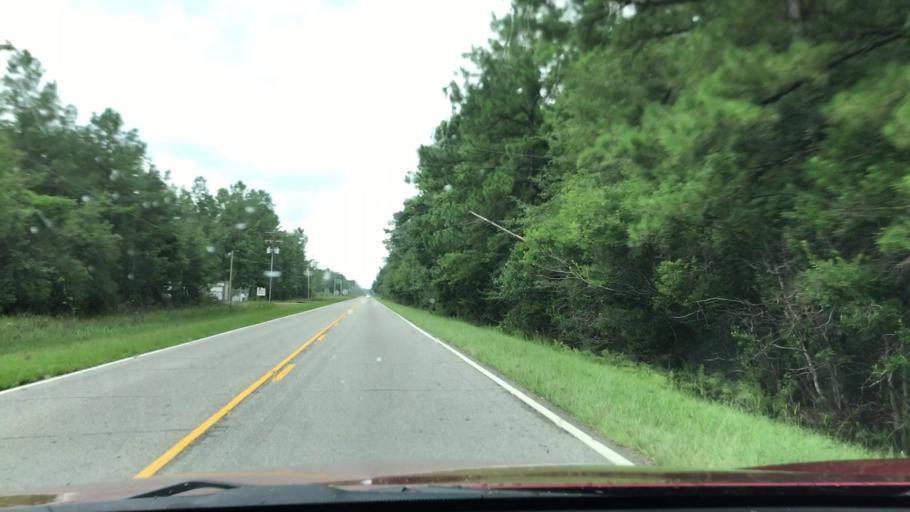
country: US
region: South Carolina
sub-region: Georgetown County
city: Georgetown
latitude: 33.5240
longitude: -79.2438
